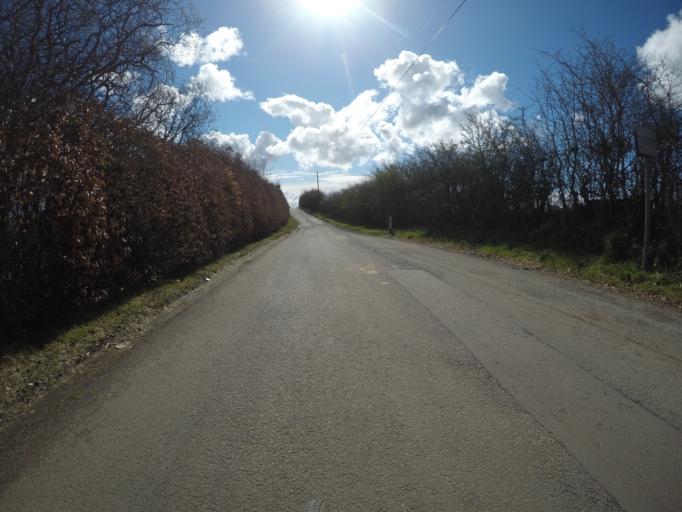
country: GB
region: Scotland
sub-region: North Ayrshire
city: Kilwinning
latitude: 55.6700
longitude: -4.7207
